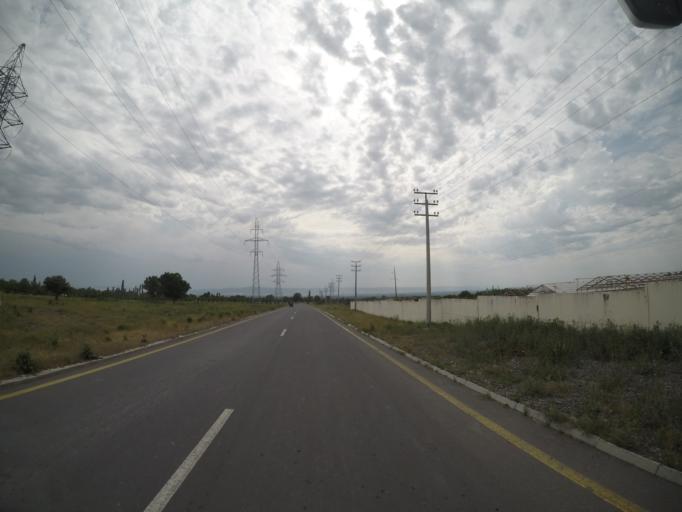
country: AZ
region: Qakh Rayon
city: Qax
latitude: 41.4132
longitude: 46.8998
